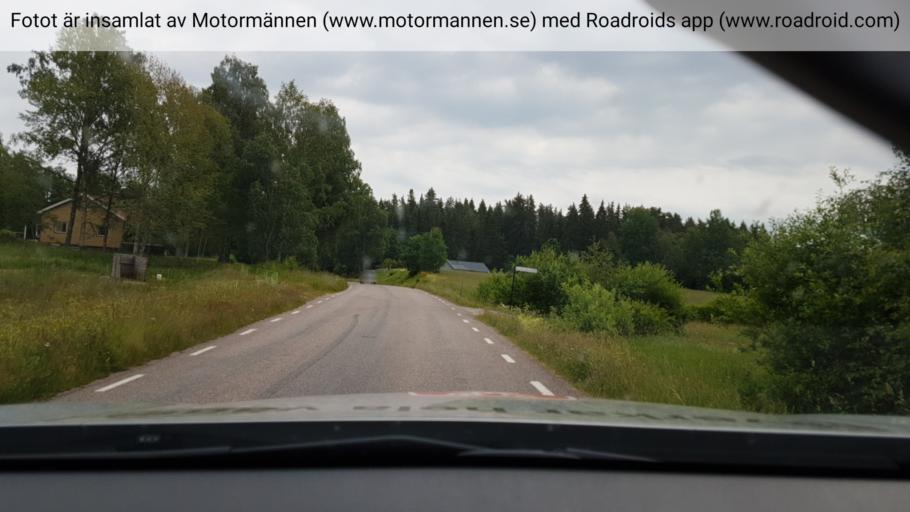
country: SE
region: Vaestra Goetaland
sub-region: Tidaholms Kommun
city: Tidaholm
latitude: 58.0707
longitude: 13.9274
